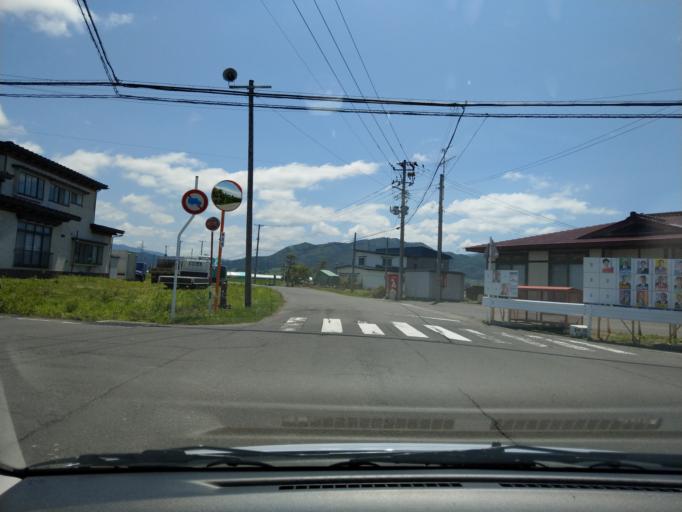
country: JP
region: Aomori
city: Hirosaki
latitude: 40.5655
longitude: 140.5515
